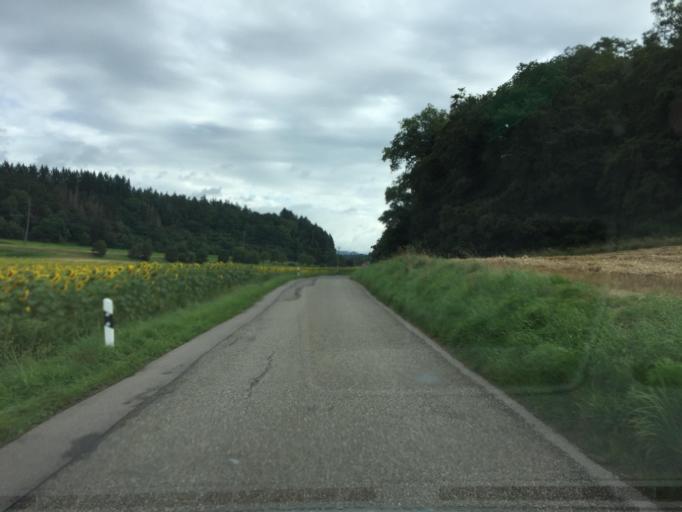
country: CH
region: Schaffhausen
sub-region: Bezirk Unterklettgau
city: Wilchingen
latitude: 47.6383
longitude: 8.4495
